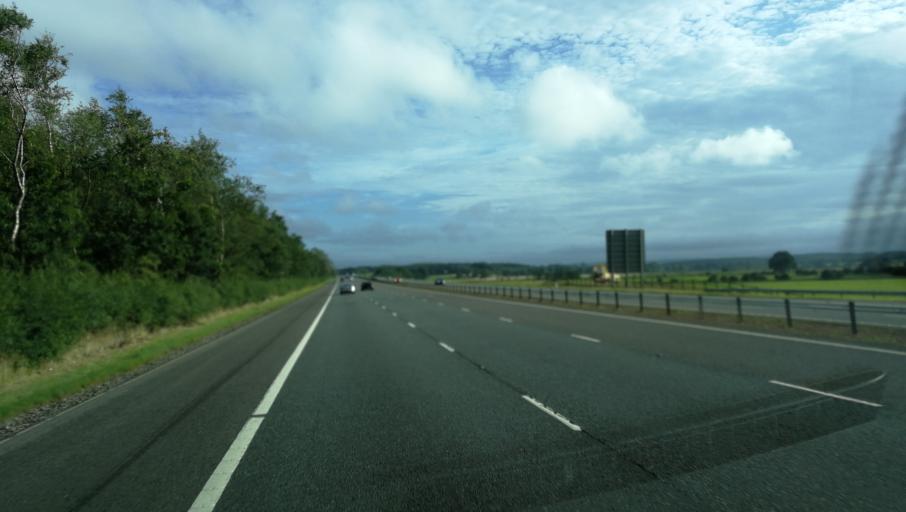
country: GB
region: Scotland
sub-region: Dumfries and Galloway
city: Lochmaben
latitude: 55.1962
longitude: -3.4098
